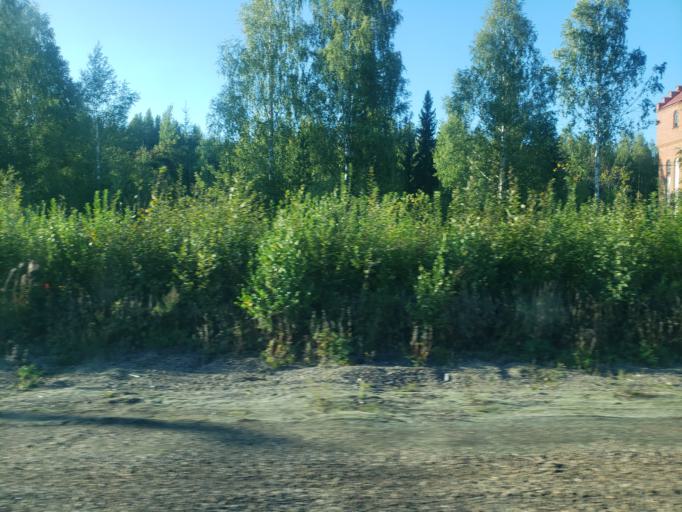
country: FI
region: South Karelia
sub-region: Lappeenranta
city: Lappeenranta
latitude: 60.9084
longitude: 28.1561
